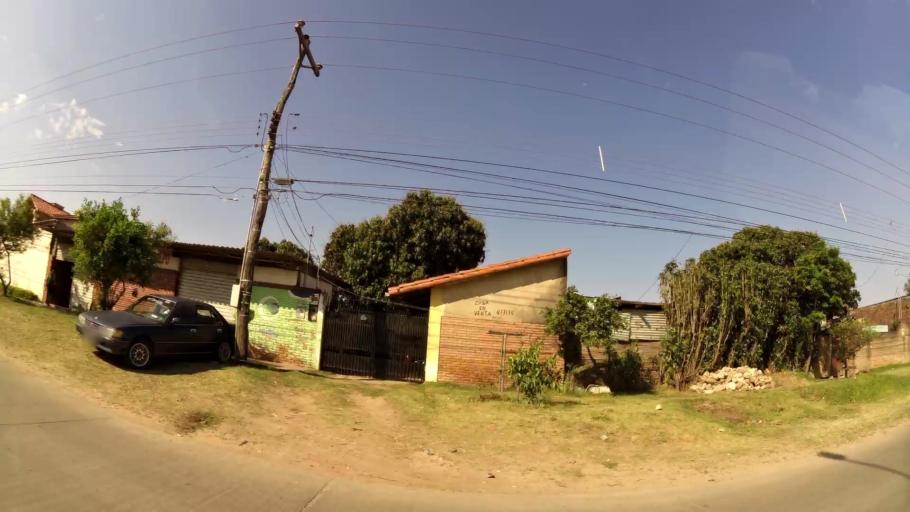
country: BO
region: Santa Cruz
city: Santa Cruz de la Sierra
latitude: -17.7978
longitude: -63.1425
